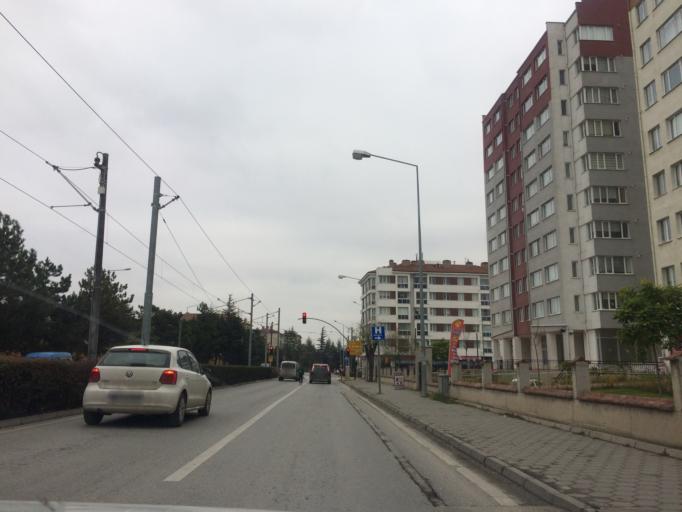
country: TR
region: Eskisehir
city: Eskisehir
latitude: 39.7898
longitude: 30.4885
